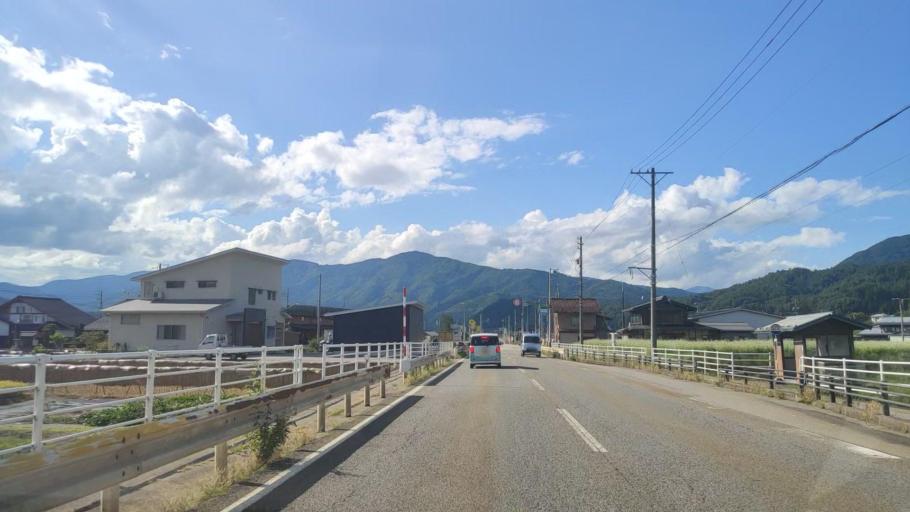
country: JP
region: Gifu
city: Takayama
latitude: 36.2550
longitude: 137.1581
